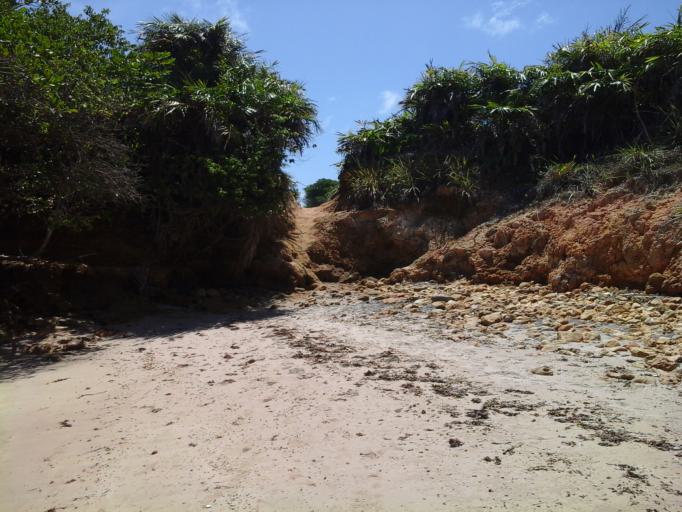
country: BR
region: Paraiba
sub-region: Pitimbu
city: Pitimbu
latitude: -7.3631
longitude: -34.7989
